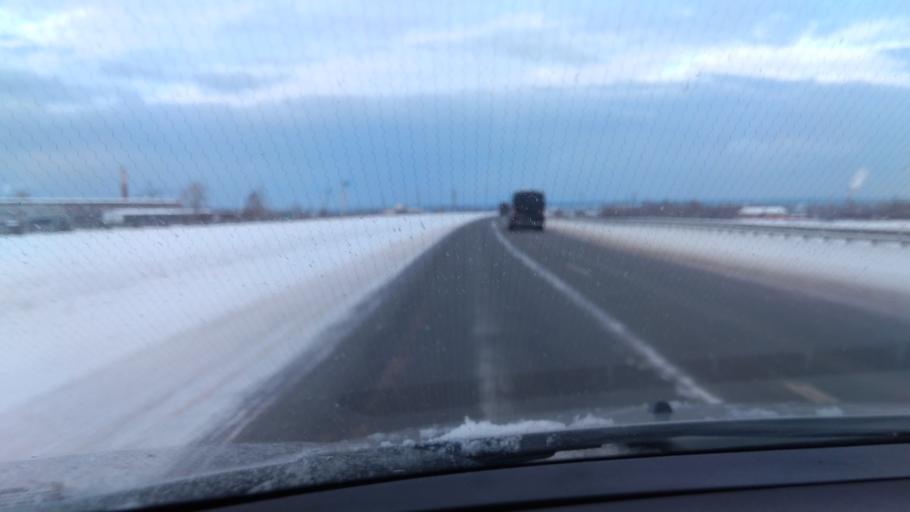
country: RU
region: Sverdlovsk
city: Tsementnyy
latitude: 57.4709
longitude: 60.1822
